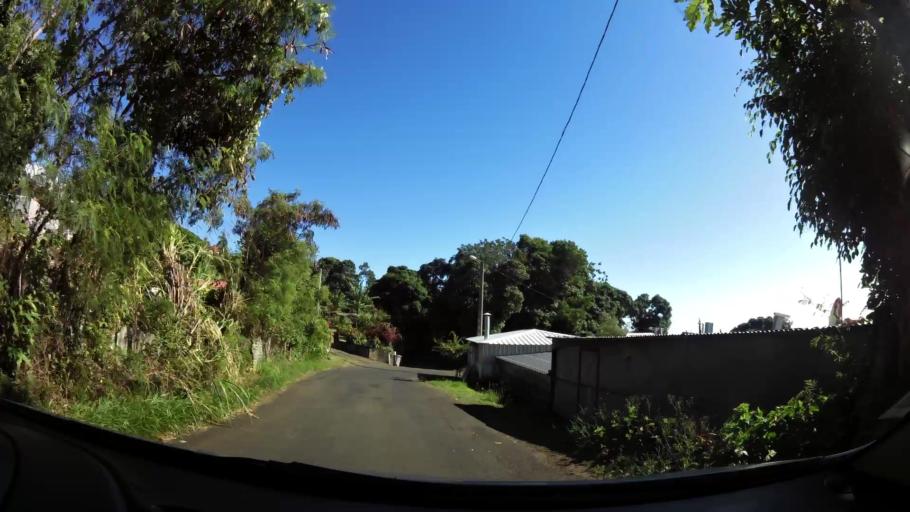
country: RE
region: Reunion
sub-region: Reunion
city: Saint-Denis
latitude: -20.9180
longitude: 55.4861
